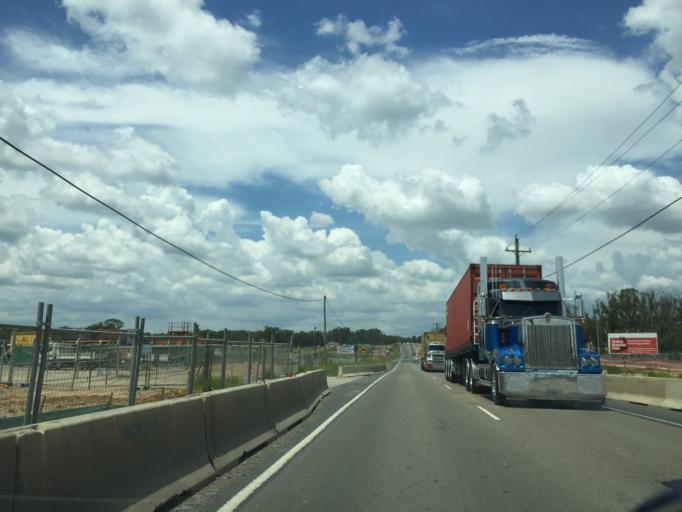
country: AU
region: New South Wales
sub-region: Blacktown
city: Hassall Grove
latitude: -33.7074
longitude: 150.8395
